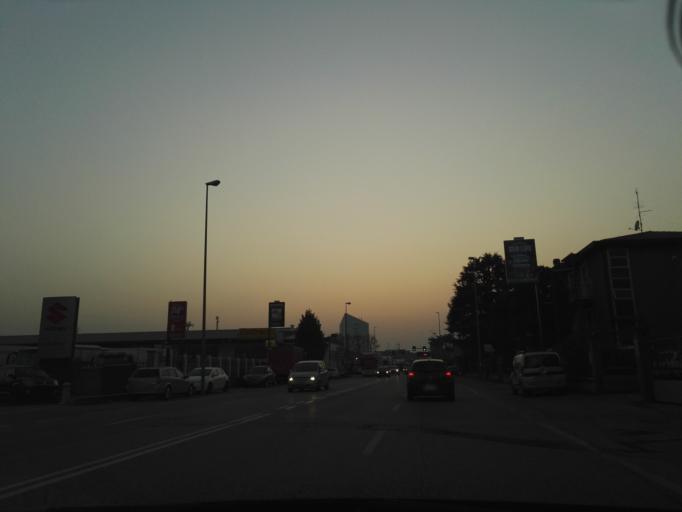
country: IT
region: Veneto
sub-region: Provincia di Verona
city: Verona
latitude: 45.4013
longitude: 10.9789
